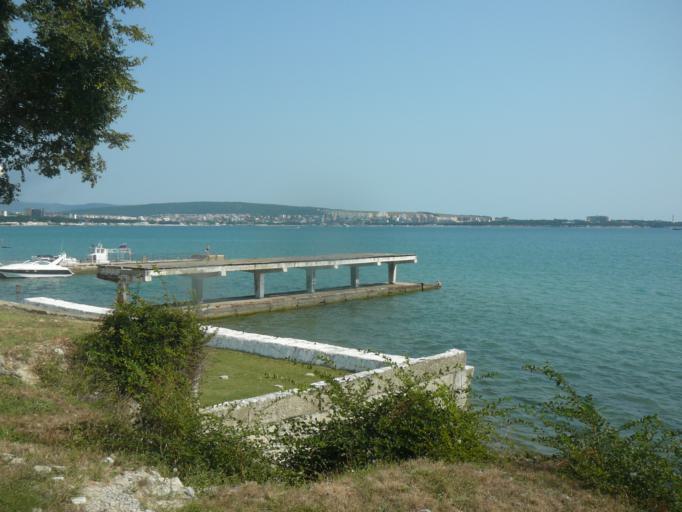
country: RU
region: Krasnodarskiy
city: Gelendzhik
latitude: 44.5856
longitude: 38.0406
